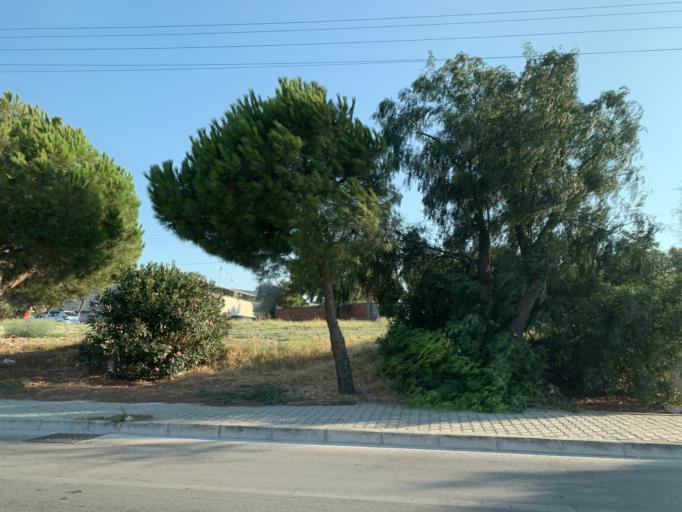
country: TR
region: Izmir
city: Alacati
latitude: 38.3088
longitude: 26.3521
